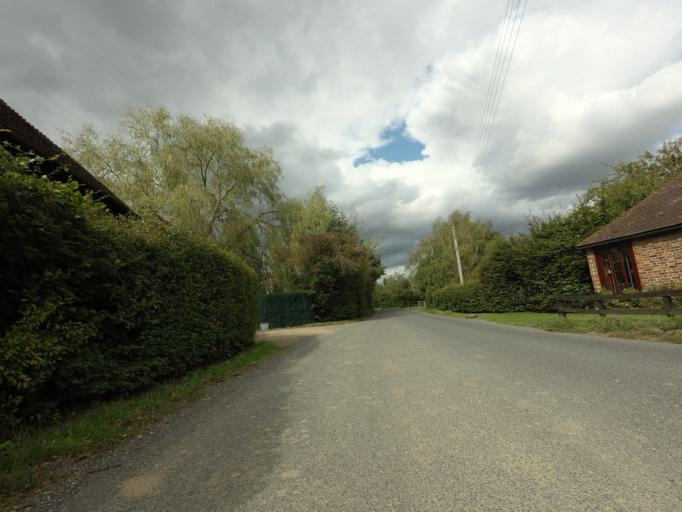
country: GB
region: England
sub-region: Kent
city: Paddock Wood
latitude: 51.1646
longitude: 0.4242
